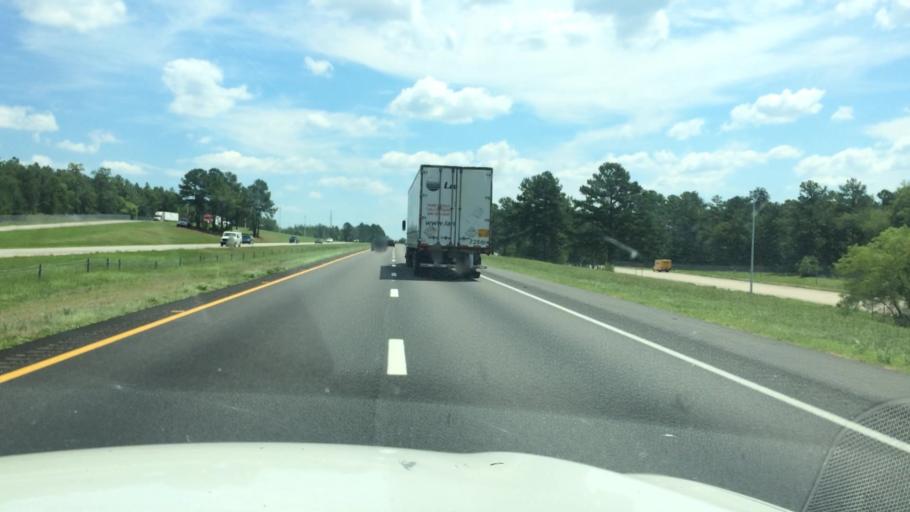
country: US
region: South Carolina
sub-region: Aiken County
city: Aiken
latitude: 33.6516
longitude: -81.7103
